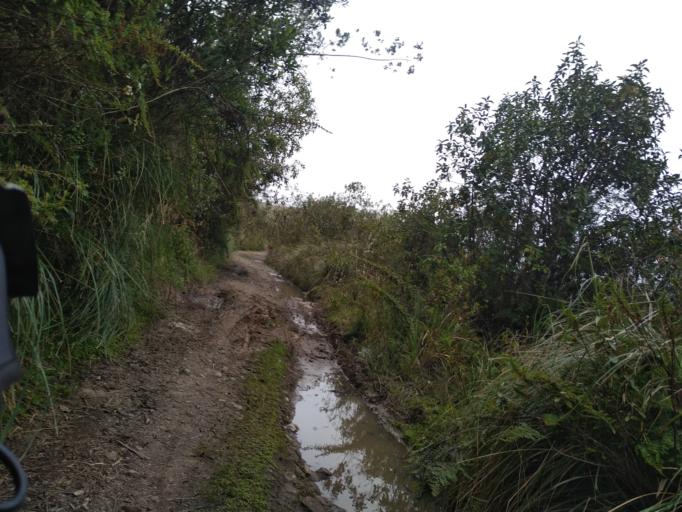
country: EC
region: Carchi
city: San Gabriel
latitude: 0.6993
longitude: -77.8437
